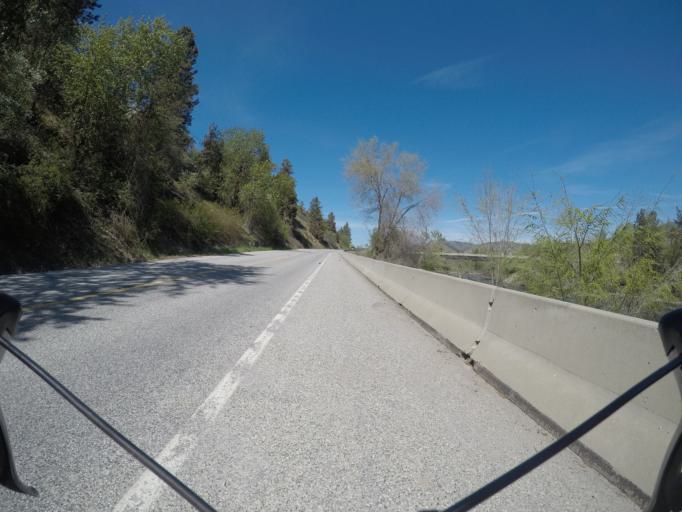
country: US
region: Washington
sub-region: Chelan County
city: Cashmere
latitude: 47.5338
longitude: -120.5501
